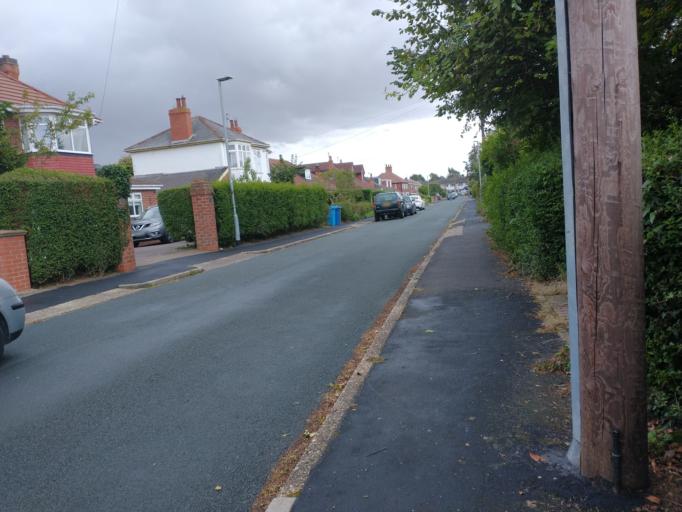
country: GB
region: England
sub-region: East Riding of Yorkshire
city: Willerby
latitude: 53.7580
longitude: -0.4364
